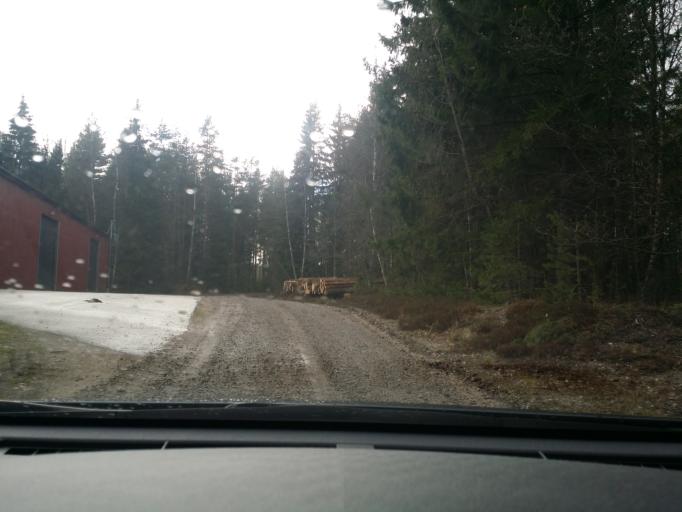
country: SE
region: Soedermanland
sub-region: Eskilstuna Kommun
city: Arla
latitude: 59.3735
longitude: 16.6577
